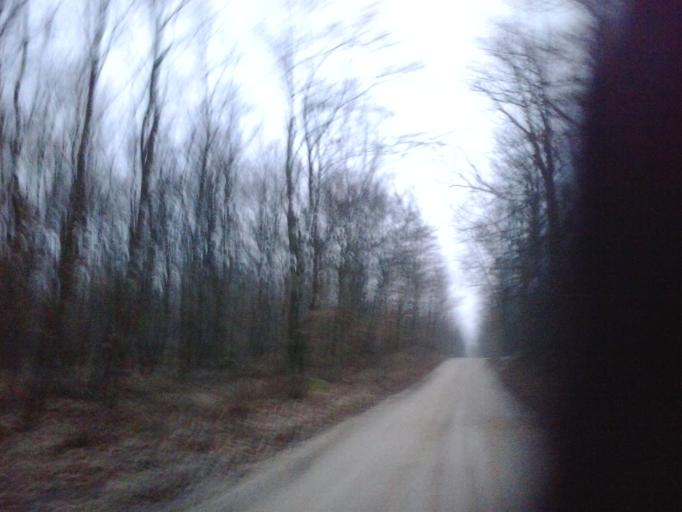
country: HU
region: Vas
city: Sarvar
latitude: 47.1372
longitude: 16.9817
